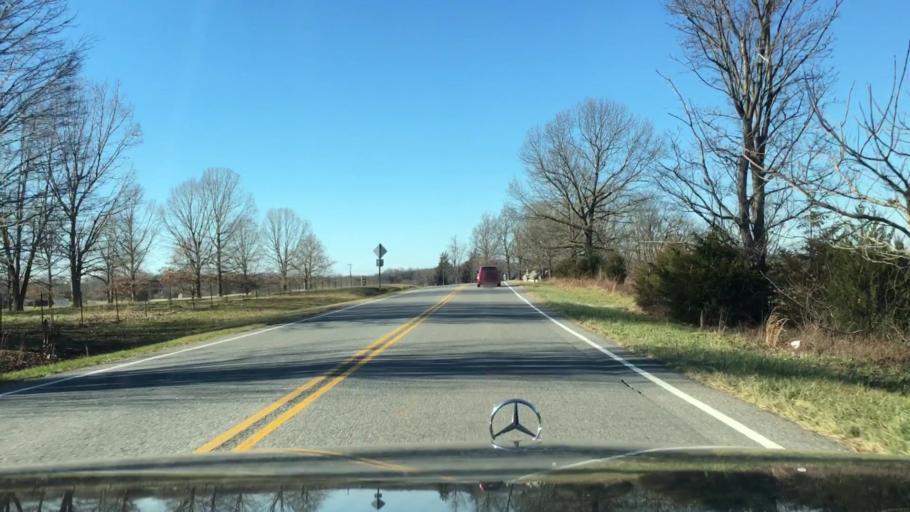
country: US
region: Virginia
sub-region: City of Bedford
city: Bedford
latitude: 37.2197
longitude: -79.4819
